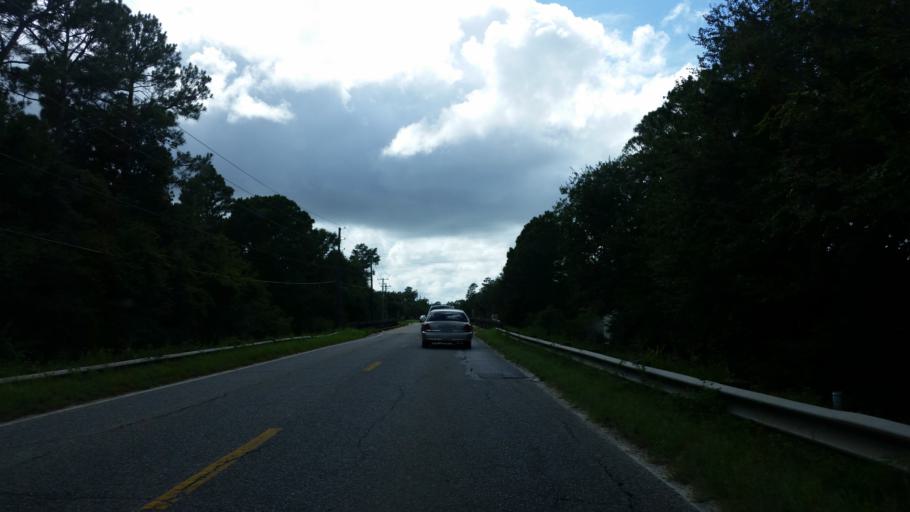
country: US
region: Florida
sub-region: Santa Rosa County
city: Holley
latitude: 30.4460
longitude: -86.9354
